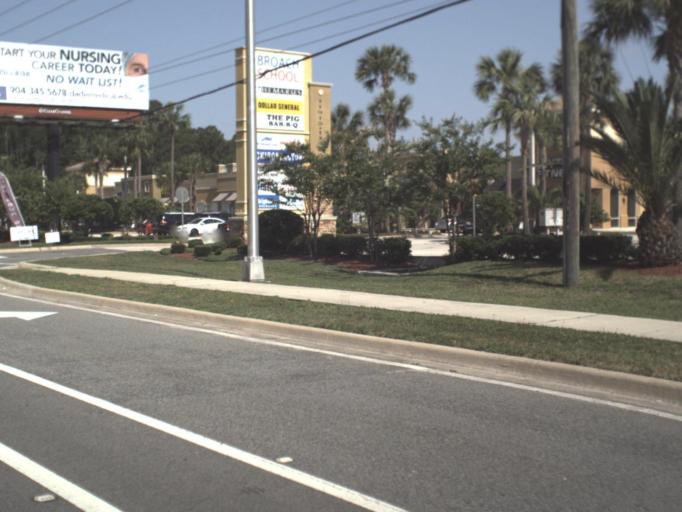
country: US
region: Florida
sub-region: Duval County
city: Neptune Beach
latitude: 30.2873
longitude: -81.5030
